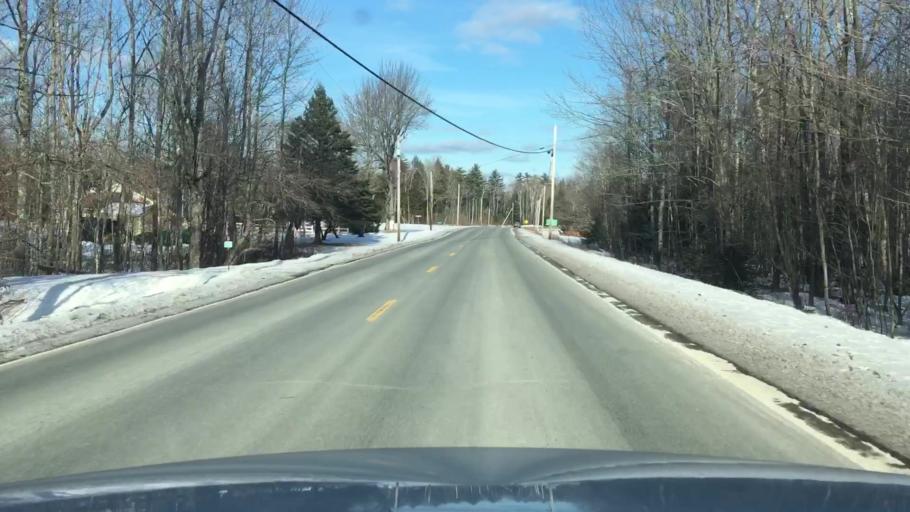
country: US
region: Maine
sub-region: Penobscot County
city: Holden
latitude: 44.7486
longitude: -68.6128
